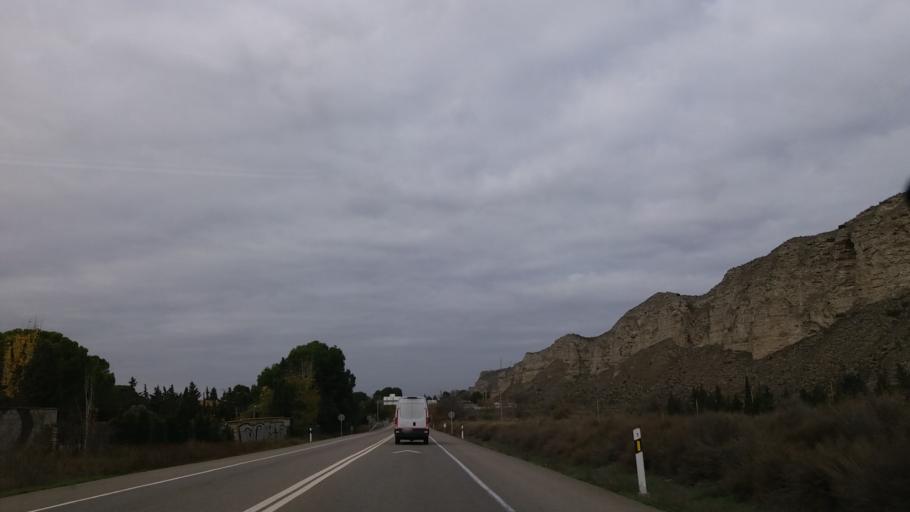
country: ES
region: Aragon
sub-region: Provincia de Zaragoza
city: Nuez de Ebro
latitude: 41.5882
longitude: -0.6639
